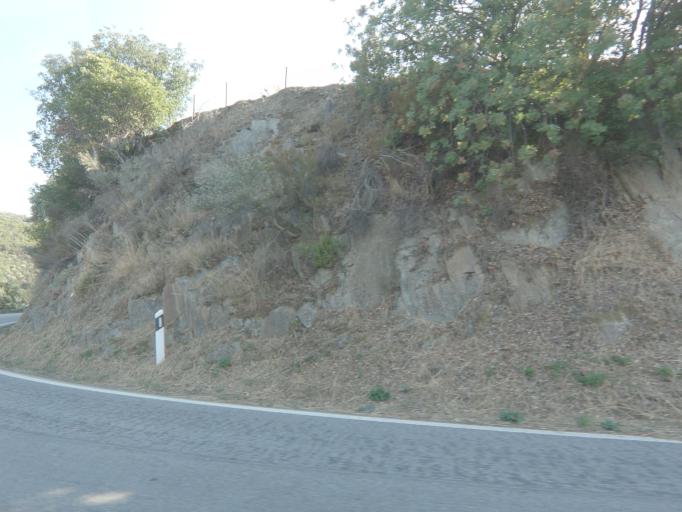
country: PT
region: Viseu
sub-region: Tabuaco
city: Tabuaco
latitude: 41.1326
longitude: -7.5712
